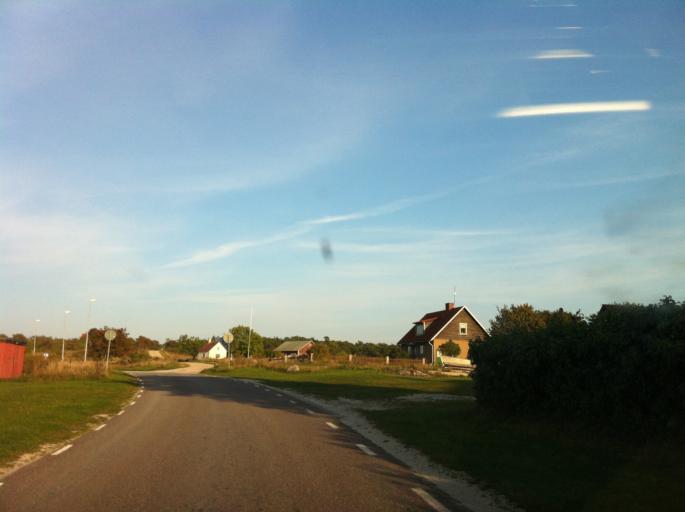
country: SE
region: Gotland
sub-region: Gotland
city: Slite
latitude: 57.4209
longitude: 18.9136
